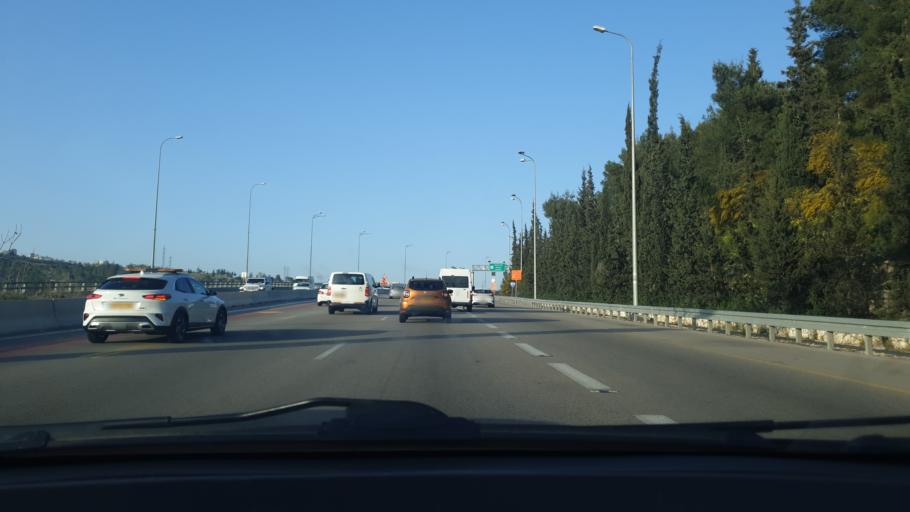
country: PS
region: West Bank
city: Bayt Iksa
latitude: 31.7989
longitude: 35.1731
